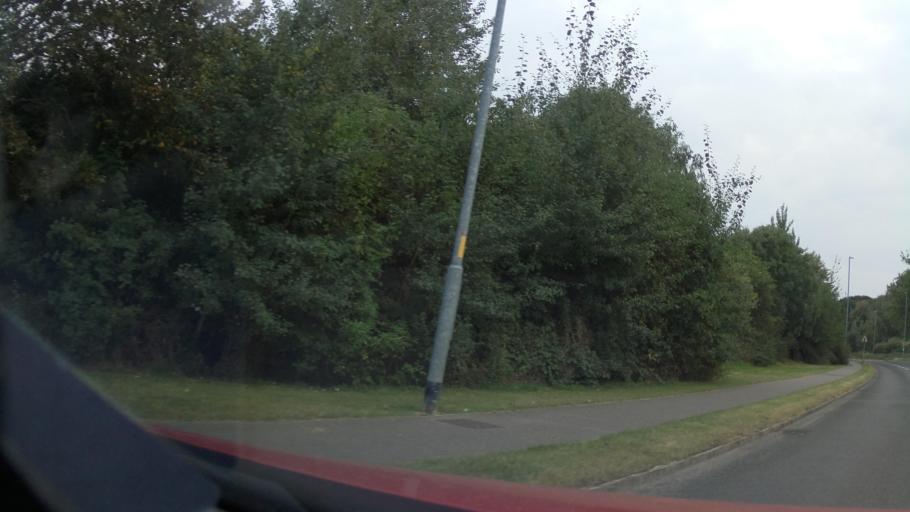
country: GB
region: England
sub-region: Nottinghamshire
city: South Collingham
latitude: 53.1486
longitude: -0.6692
